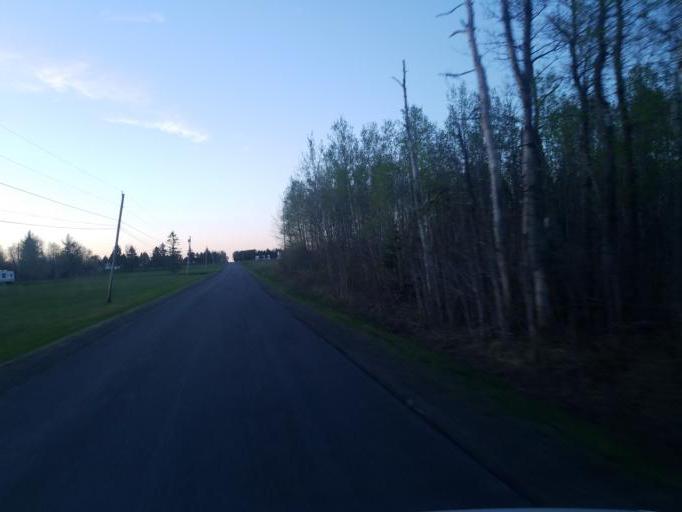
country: US
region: Maine
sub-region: Aroostook County
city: Caribou
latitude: 46.8456
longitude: -68.0704
